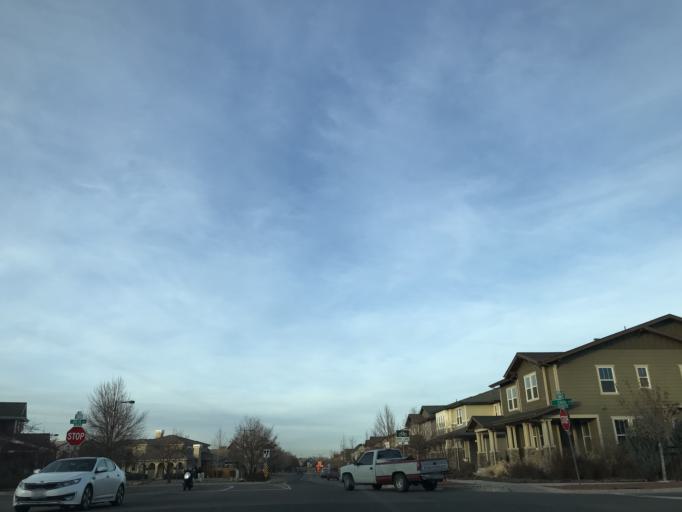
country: US
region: Colorado
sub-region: Adams County
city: Aurora
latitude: 39.7553
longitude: -104.8646
